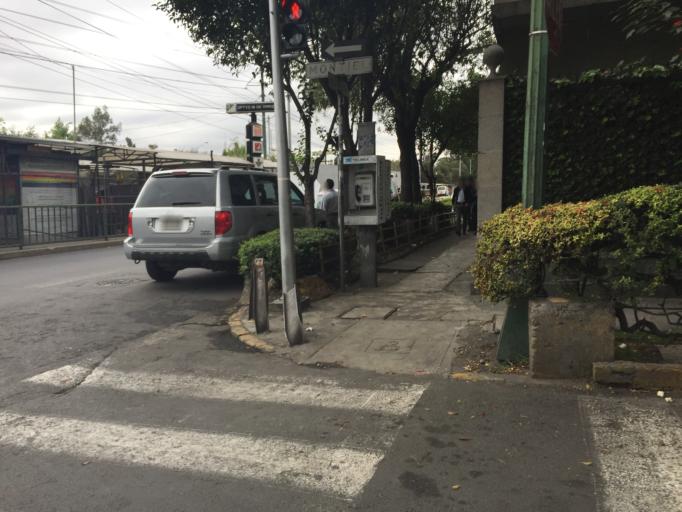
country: MX
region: Mexico
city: Colonia Lindavista
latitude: 19.4860
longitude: -99.1258
